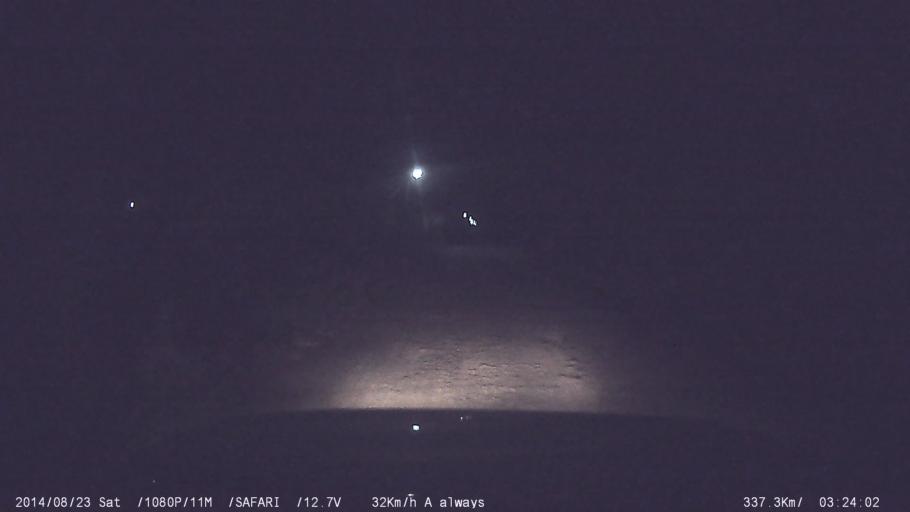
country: IN
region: Tamil Nadu
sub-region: Kancheepuram
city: Vengavasal
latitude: 12.8161
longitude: 80.2249
